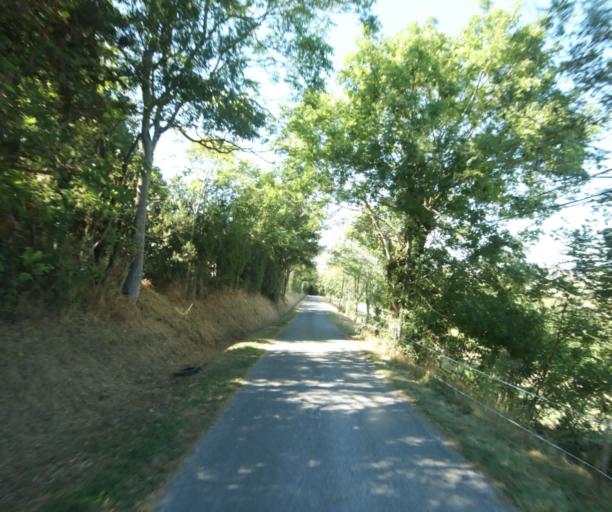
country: FR
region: Midi-Pyrenees
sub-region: Departement de la Haute-Garonne
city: Saint-Felix-Lauragais
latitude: 43.5119
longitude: 1.9346
